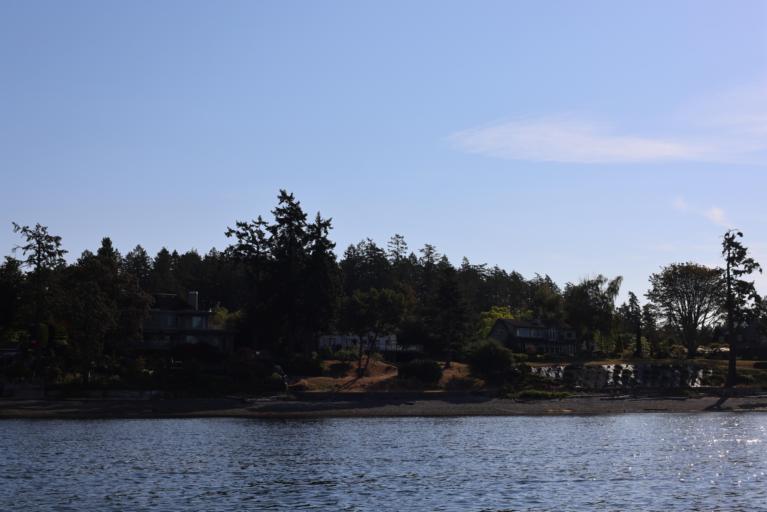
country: CA
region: British Columbia
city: North Saanich
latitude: 48.6869
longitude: -123.4759
